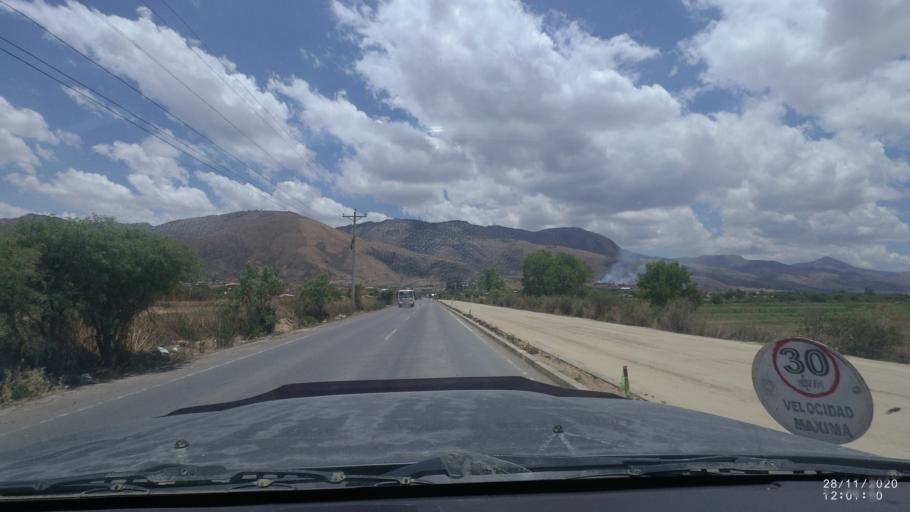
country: BO
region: Cochabamba
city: Tarata
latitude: -17.5490
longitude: -66.0064
